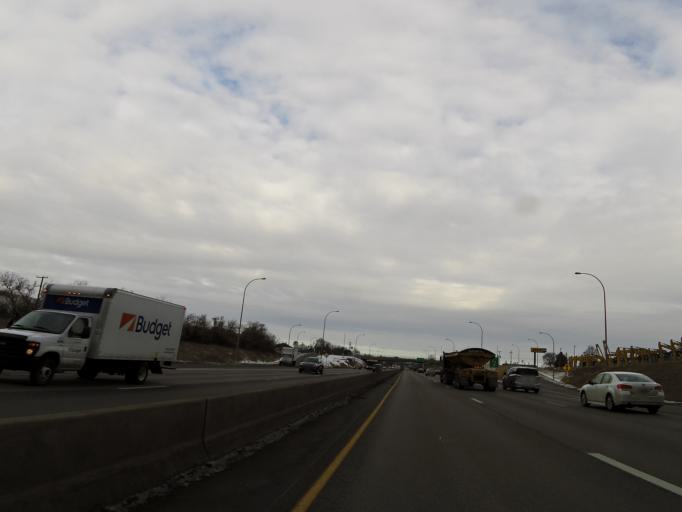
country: US
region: Minnesota
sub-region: Hennepin County
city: Bloomington
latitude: 44.8307
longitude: -93.2932
